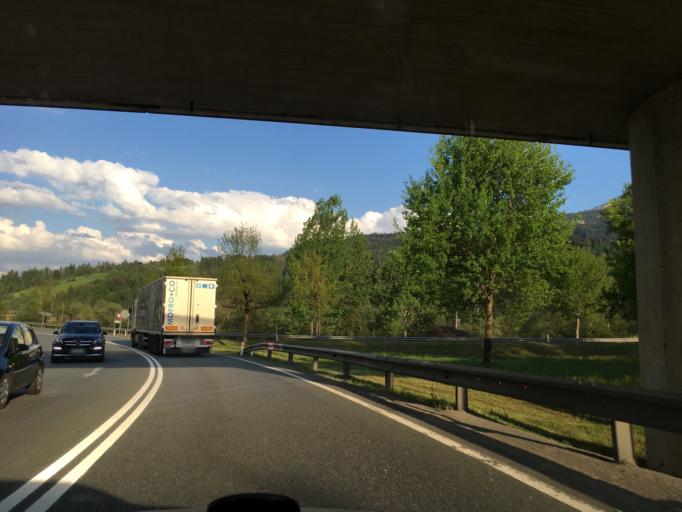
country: AT
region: Tyrol
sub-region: Politischer Bezirk Kitzbuhel
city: Sankt Johann in Tirol
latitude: 47.5170
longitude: 12.4094
